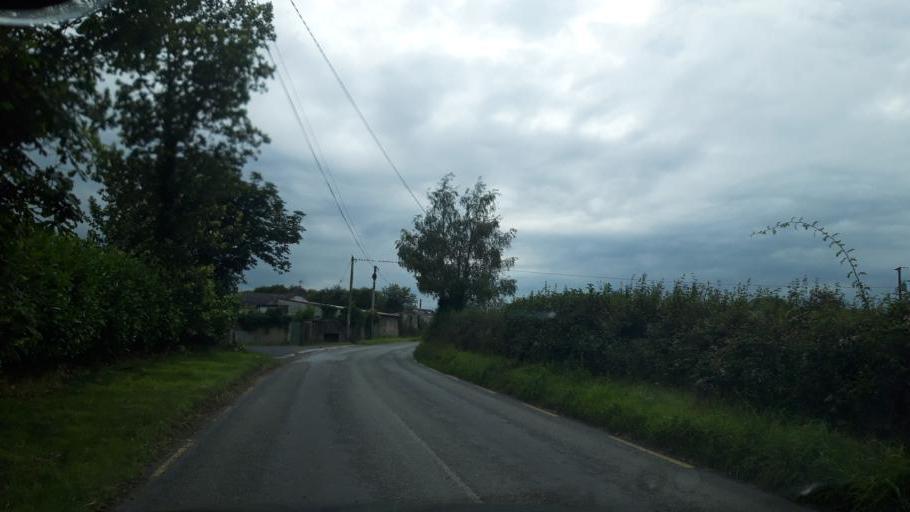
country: IE
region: Leinster
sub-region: Kilkenny
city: Ballyragget
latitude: 52.7441
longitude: -7.3965
